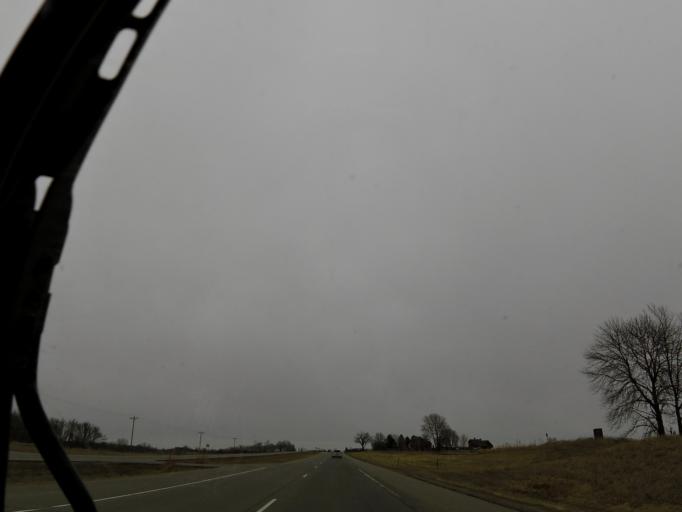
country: US
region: Minnesota
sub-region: Le Sueur County
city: Le Sueur
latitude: 44.5046
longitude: -93.8607
